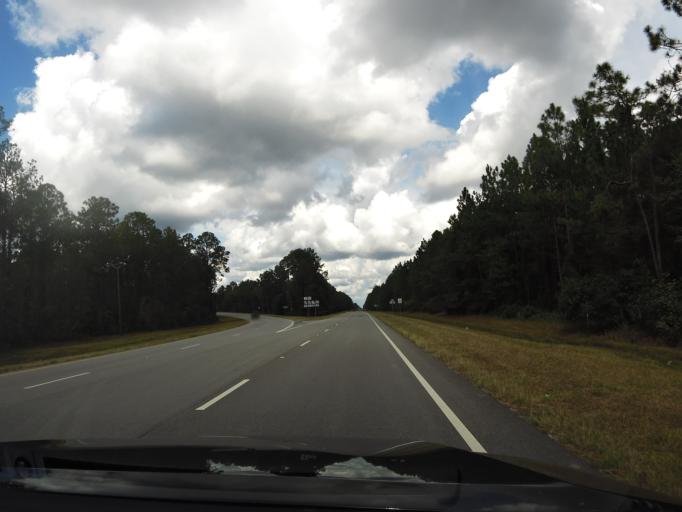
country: US
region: Georgia
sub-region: Charlton County
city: Folkston
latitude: 30.8683
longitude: -82.0121
